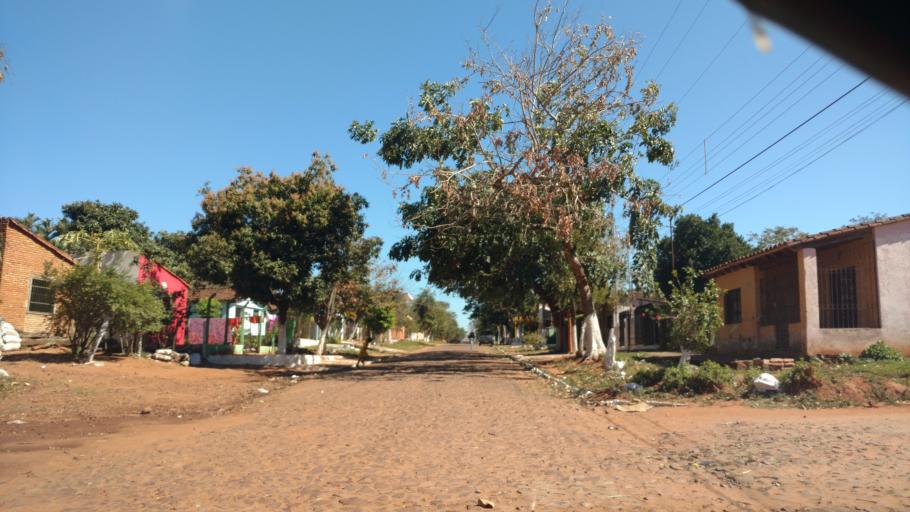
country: PY
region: Paraguari
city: Yaguaron
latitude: -25.5636
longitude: -57.2923
